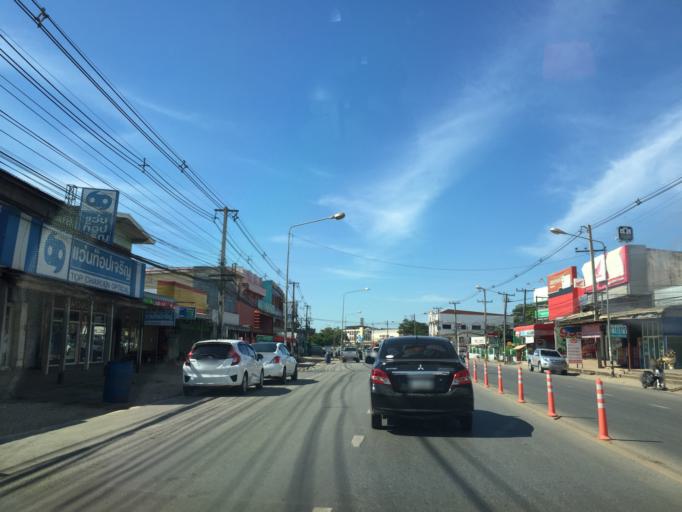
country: TH
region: Changwat Nong Bua Lamphu
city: Na Klang
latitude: 17.3016
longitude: 102.2044
